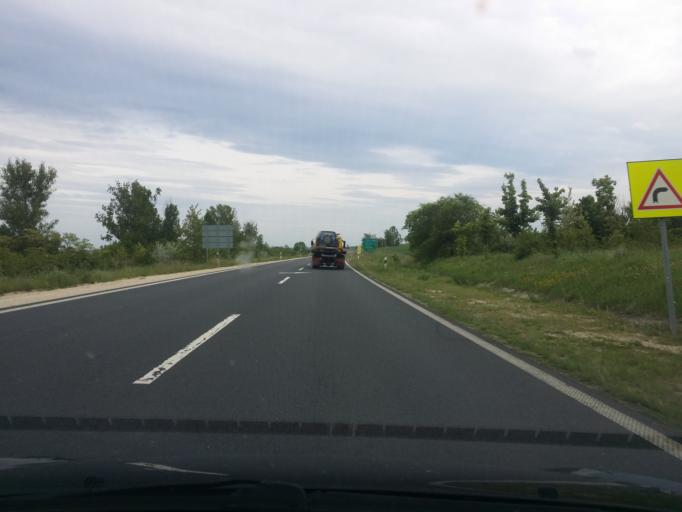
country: HU
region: Fejer
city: Lepseny
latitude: 47.0211
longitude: 18.1832
